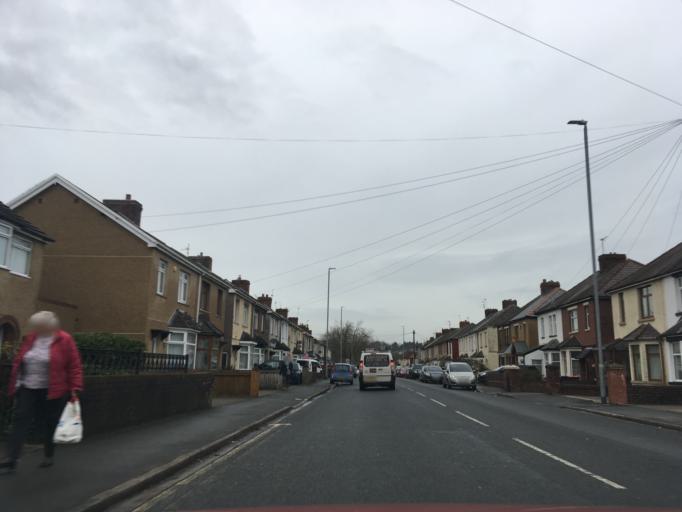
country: GB
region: Wales
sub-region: Newport
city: Nash
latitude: 51.5776
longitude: -2.9558
